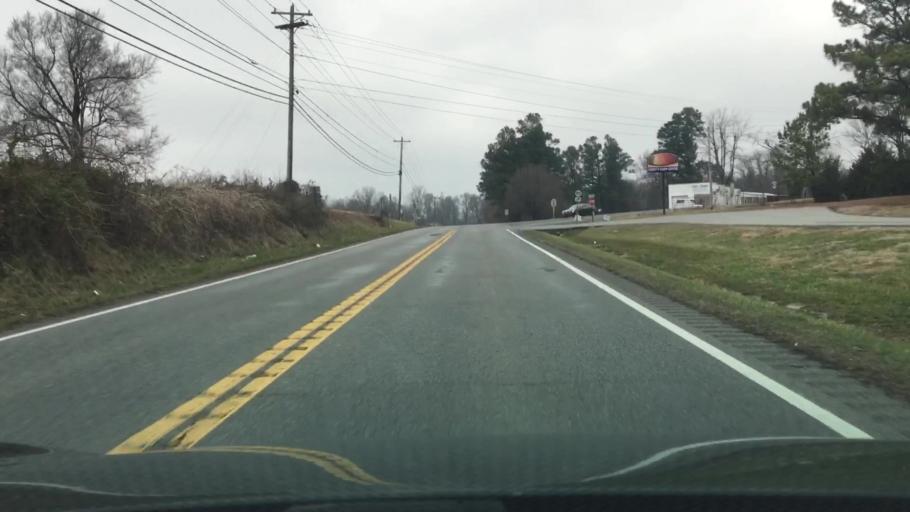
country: US
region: Kentucky
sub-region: Marshall County
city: Calvert City
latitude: 36.9462
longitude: -88.3652
